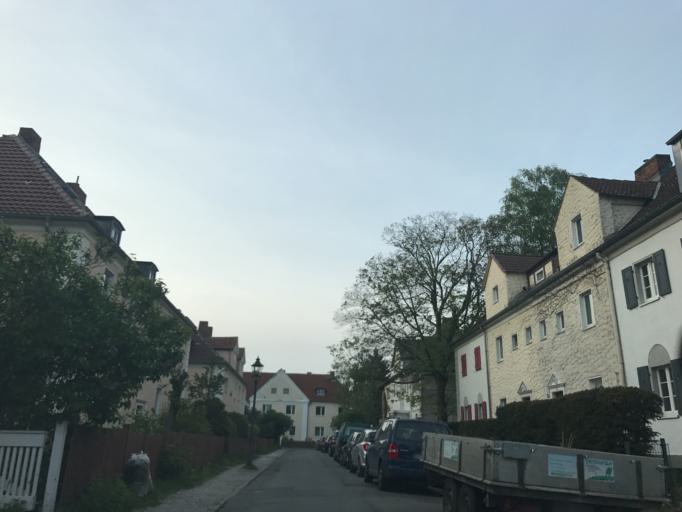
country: DE
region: Berlin
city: Westend
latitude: 52.5055
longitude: 13.2621
